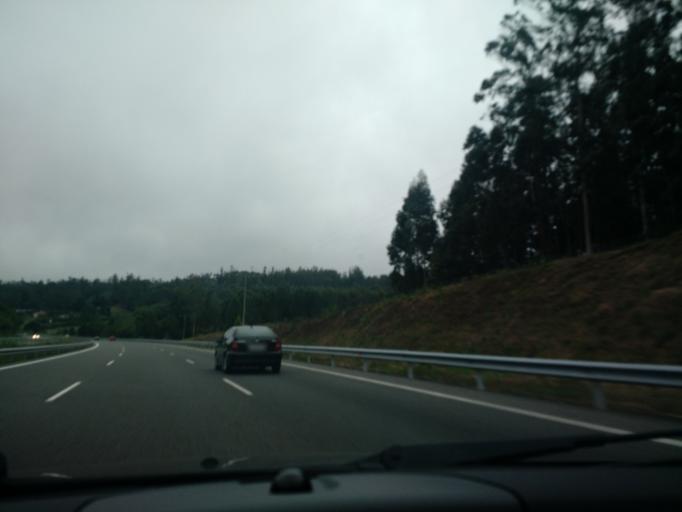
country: ES
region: Galicia
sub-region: Provincia da Coruna
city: Abegondo
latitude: 43.1953
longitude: -8.3063
